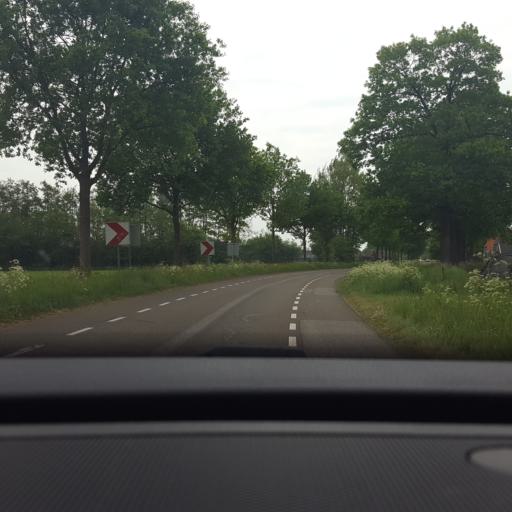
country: NL
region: Gelderland
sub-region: Gemeente Lochem
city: Barchem
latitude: 52.0519
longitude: 6.4514
